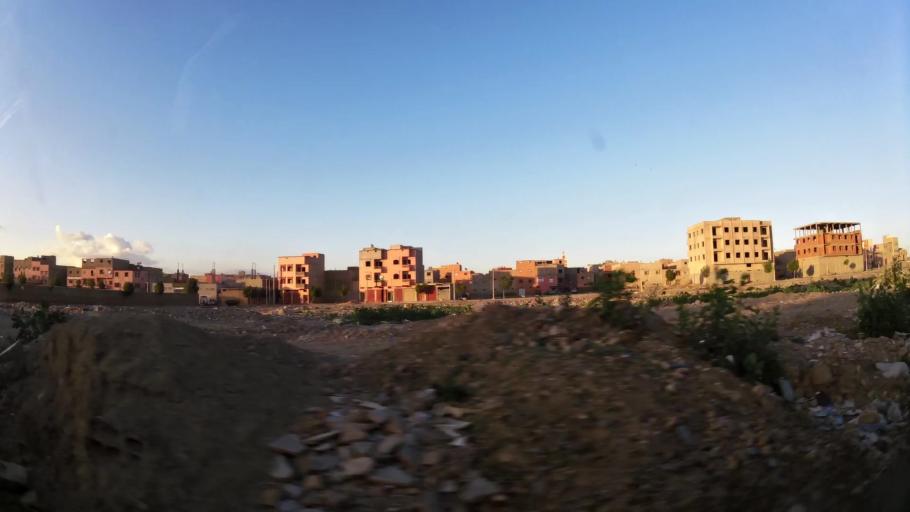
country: MA
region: Marrakech-Tensift-Al Haouz
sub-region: Kelaa-Des-Sraghna
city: Sidi Abdallah
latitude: 32.2412
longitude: -7.9428
